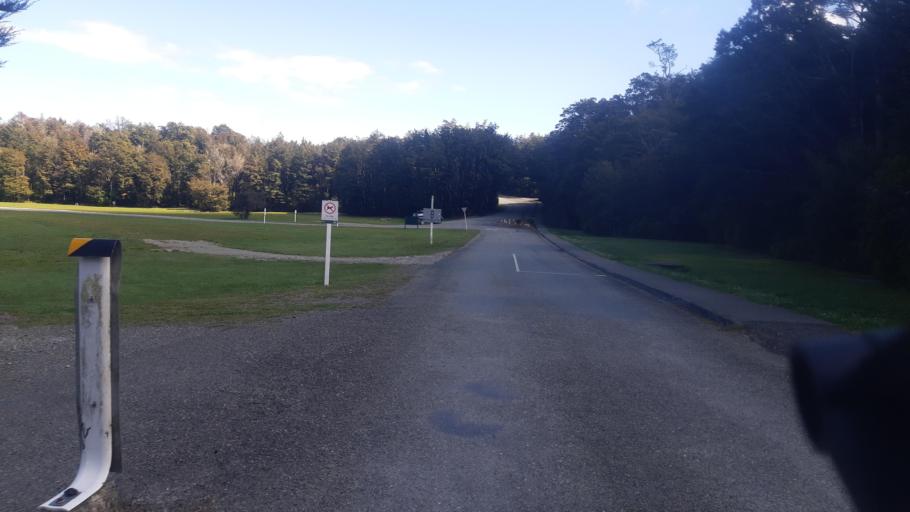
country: NZ
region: Tasman
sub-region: Tasman District
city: Wakefield
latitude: -41.8064
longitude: 172.8463
